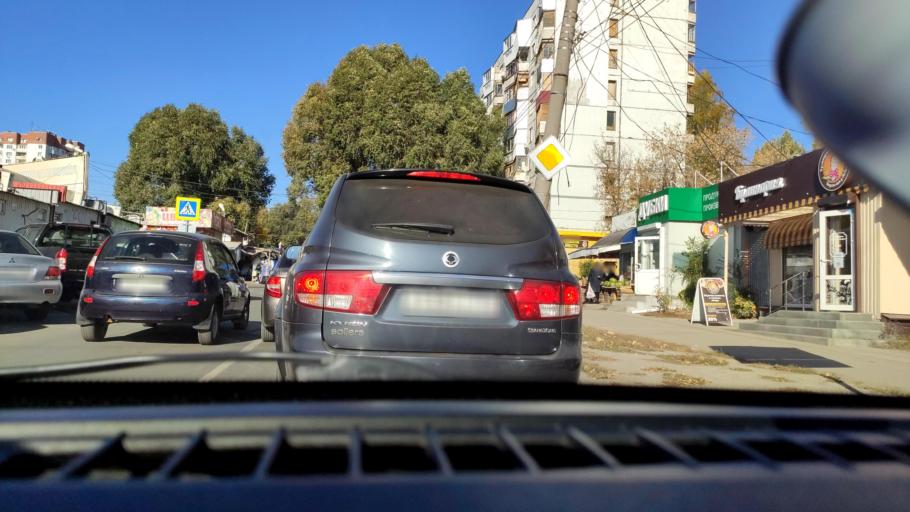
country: RU
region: Samara
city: Samara
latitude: 53.2461
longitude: 50.2513
